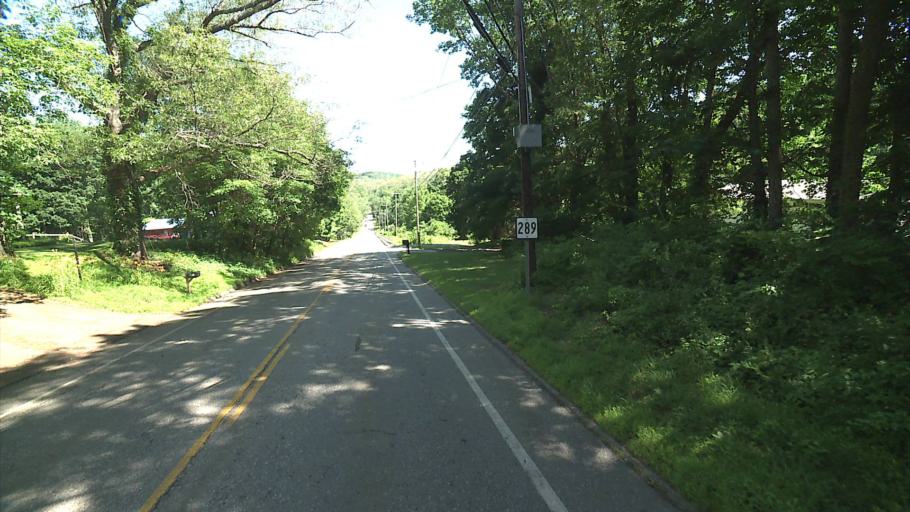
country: US
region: Connecticut
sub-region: Windham County
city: Willimantic
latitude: 41.6522
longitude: -72.2266
